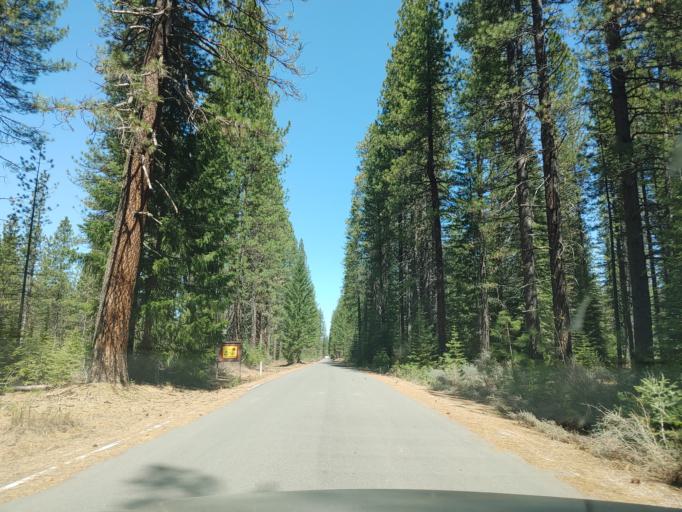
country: US
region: California
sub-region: Siskiyou County
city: McCloud
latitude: 41.2600
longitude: -121.9426
